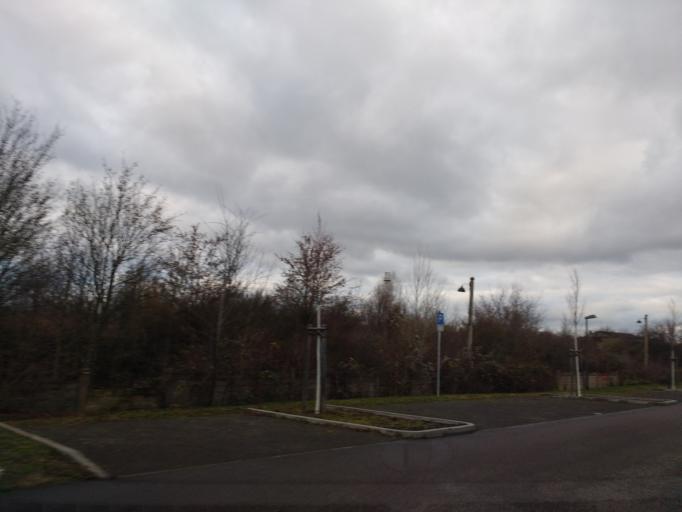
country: DE
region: Saxony-Anhalt
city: Braunsbedra
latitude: 51.2942
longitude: 11.8685
